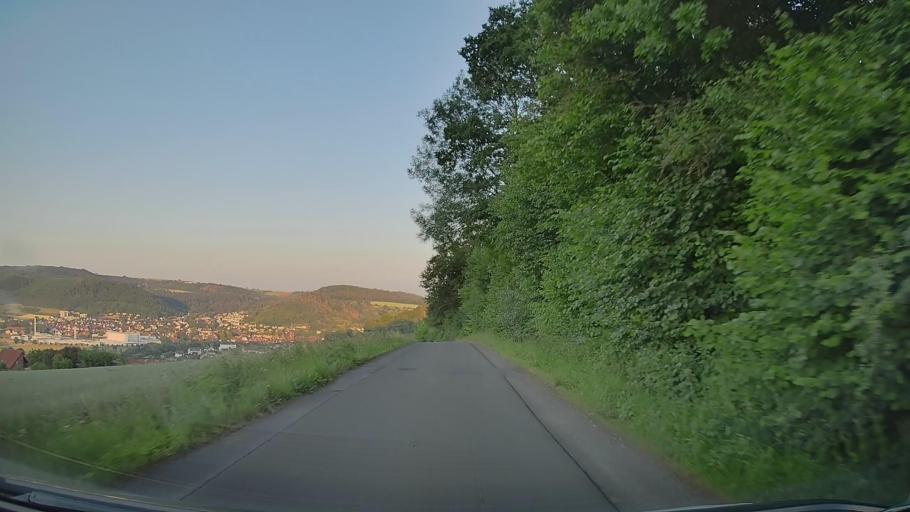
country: DE
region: North Rhine-Westphalia
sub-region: Regierungsbezirk Detmold
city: Lugde
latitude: 51.9651
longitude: 9.2259
